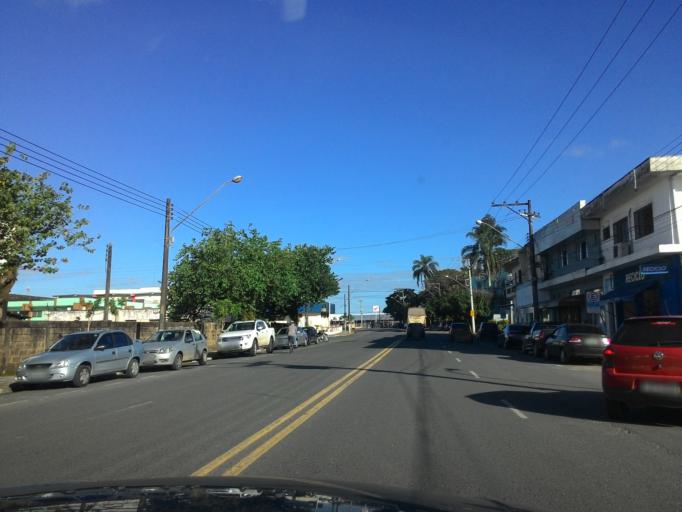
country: BR
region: Sao Paulo
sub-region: Registro
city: Registro
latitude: -24.4988
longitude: -47.8475
